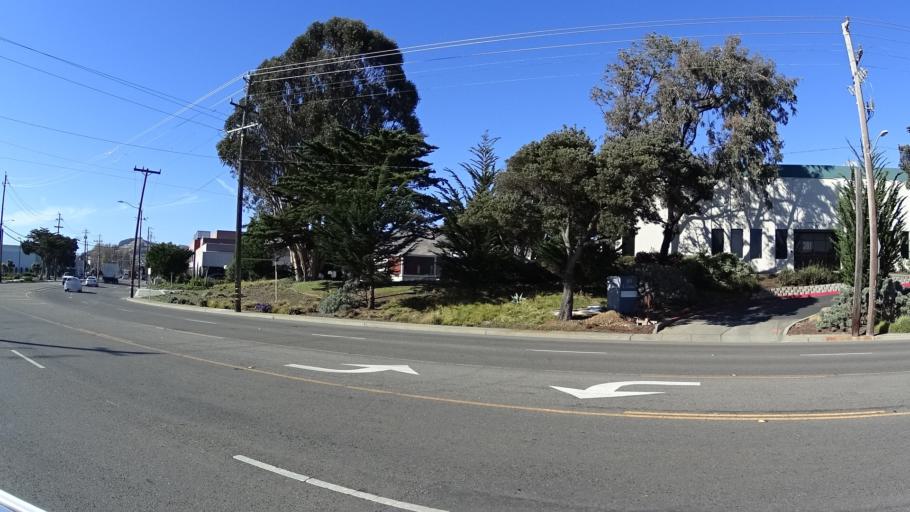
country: US
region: California
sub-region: San Mateo County
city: South San Francisco
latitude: 37.6516
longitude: -122.3917
